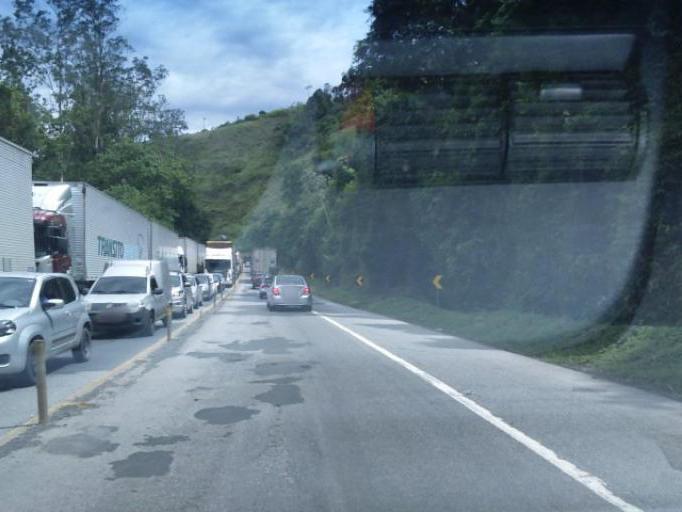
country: BR
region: Sao Paulo
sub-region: Miracatu
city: Miracatu
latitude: -24.1140
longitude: -47.2699
